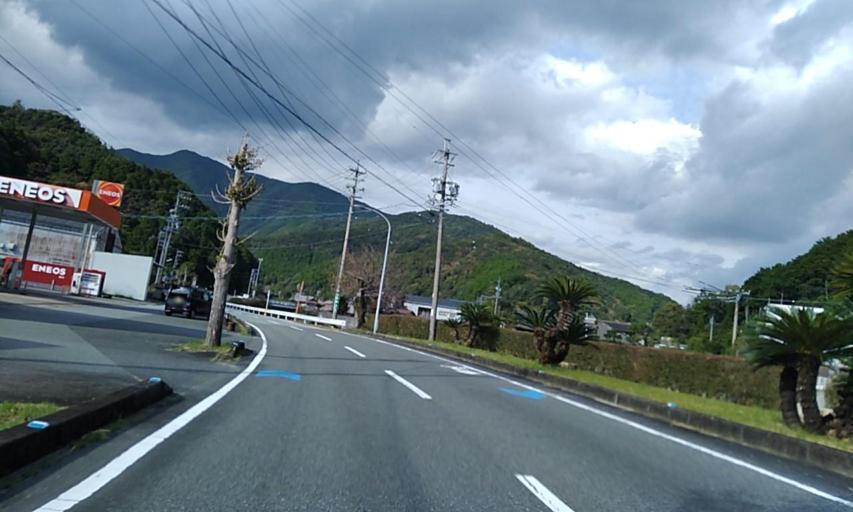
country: JP
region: Mie
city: Owase
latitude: 34.2269
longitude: 136.3946
